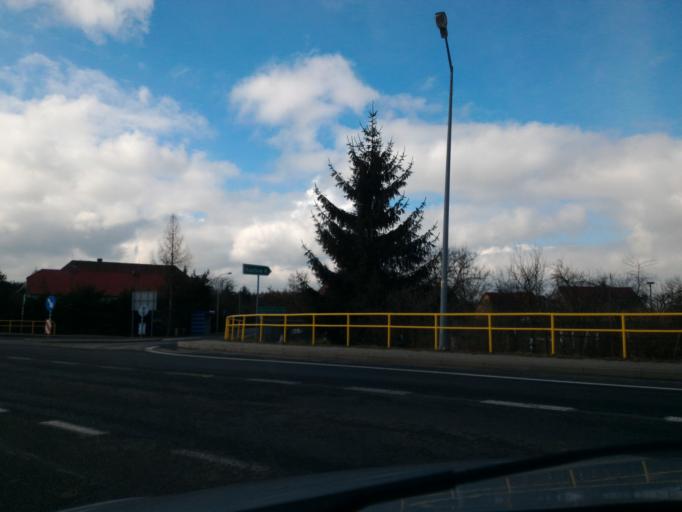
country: PL
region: Lower Silesian Voivodeship
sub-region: Powiat zgorzelecki
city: Sulikow
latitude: 51.0681
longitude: 15.0066
